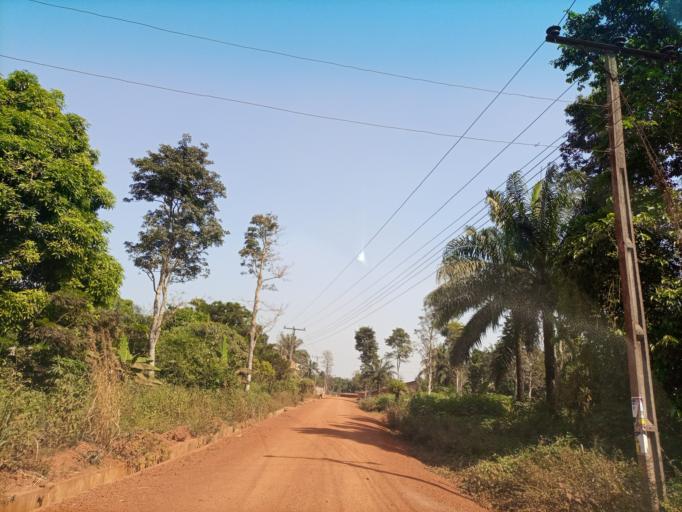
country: NG
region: Enugu
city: Nsukka
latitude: 6.7994
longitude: 7.3505
